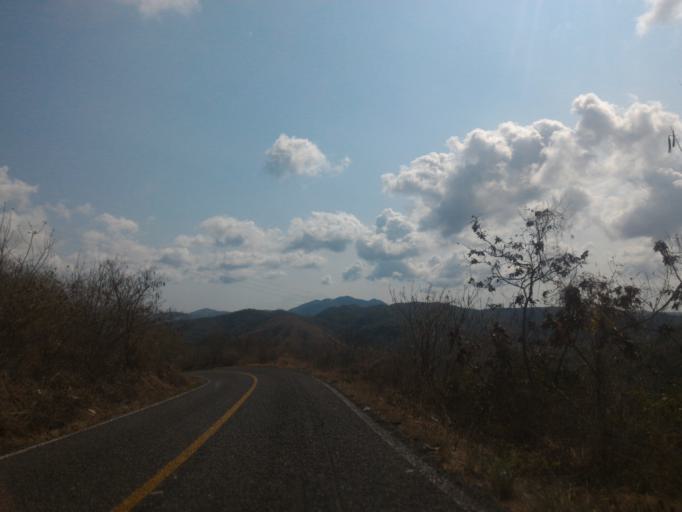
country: MX
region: Michoacan
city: Coahuayana Viejo
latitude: 18.4633
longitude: -103.5526
